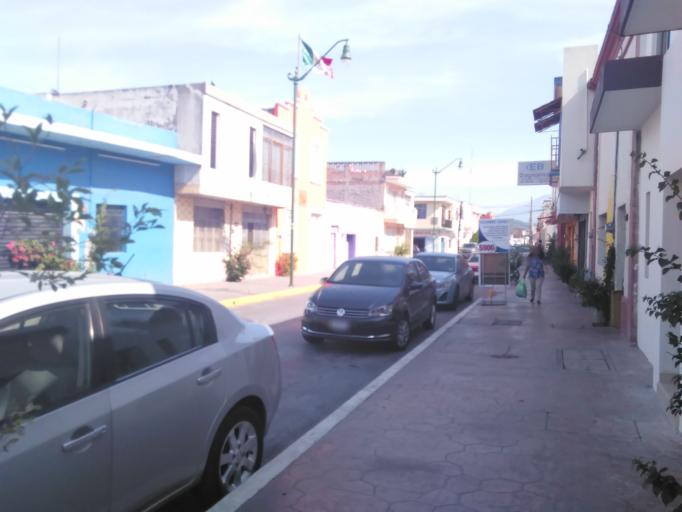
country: MX
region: Nayarit
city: Tepic
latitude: 21.5130
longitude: -104.8977
